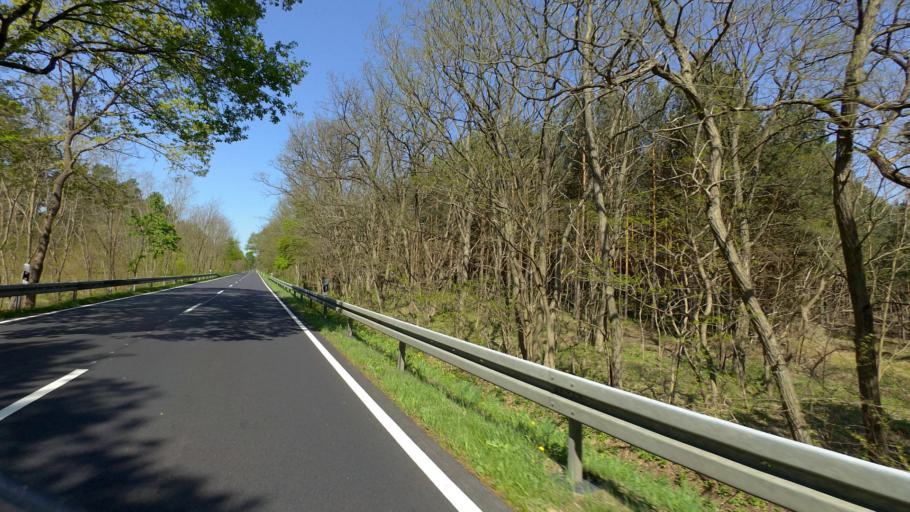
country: DE
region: Brandenburg
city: Lieberose
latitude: 52.0079
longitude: 14.3098
